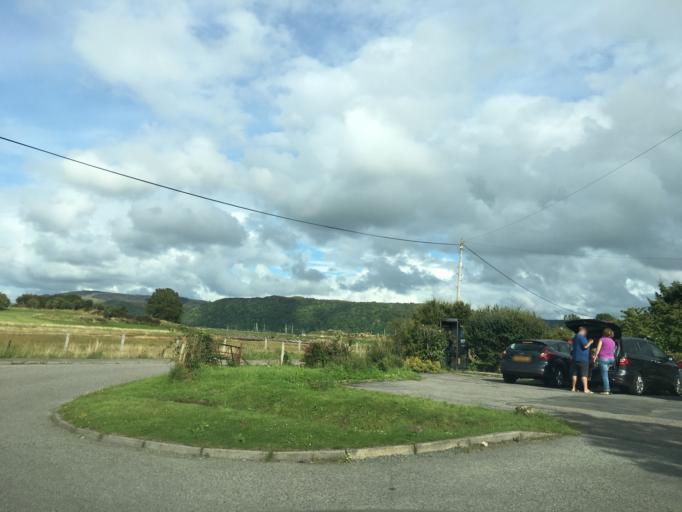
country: GB
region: Scotland
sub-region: Argyll and Bute
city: Oban
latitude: 56.2923
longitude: -5.6138
